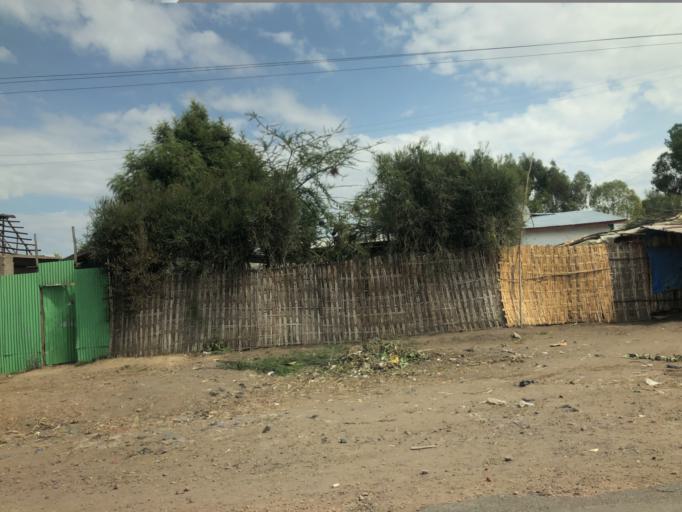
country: ET
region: Oromiya
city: Shashemene
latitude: 7.3712
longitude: 38.6715
